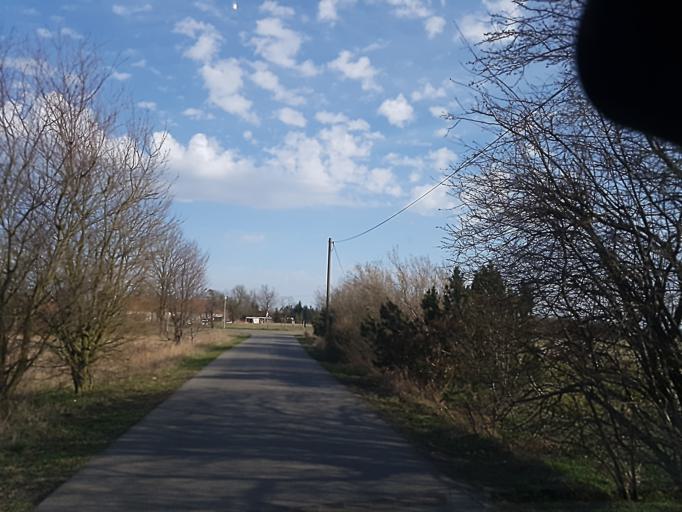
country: DE
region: Brandenburg
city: Muhlberg
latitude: 51.4742
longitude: 13.2656
